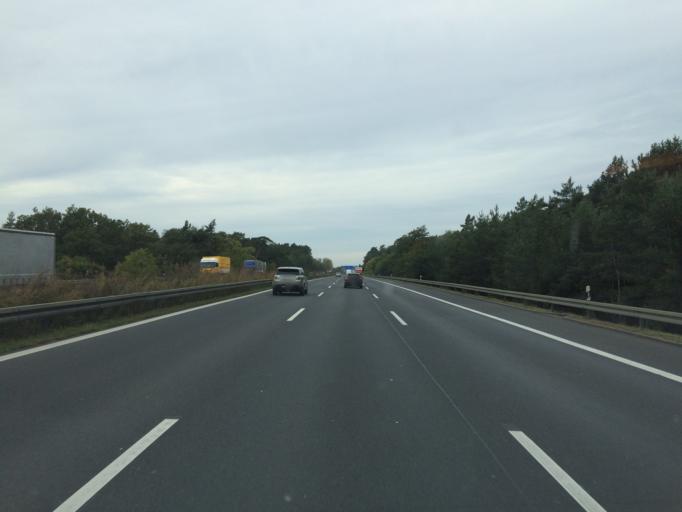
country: DE
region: Brandenburg
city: Michendorf
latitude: 52.3026
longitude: 13.1201
